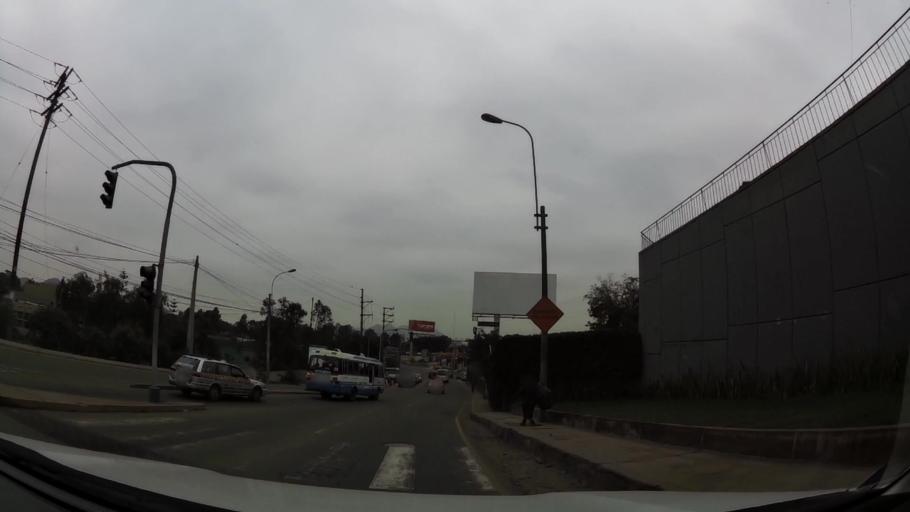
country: PE
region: Lima
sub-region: Lima
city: La Molina
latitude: -12.0762
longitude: -76.9344
